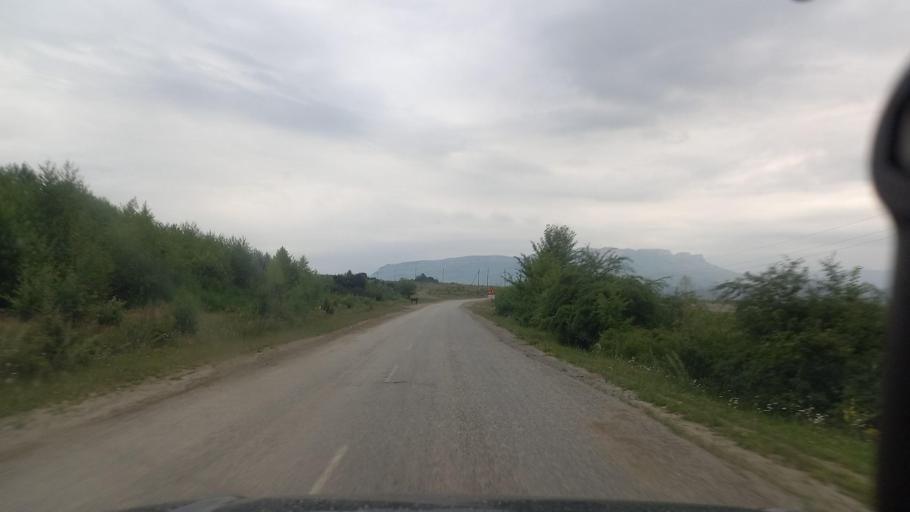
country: RU
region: Karachayevo-Cherkesiya
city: Pregradnaya
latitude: 43.9437
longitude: 41.1561
